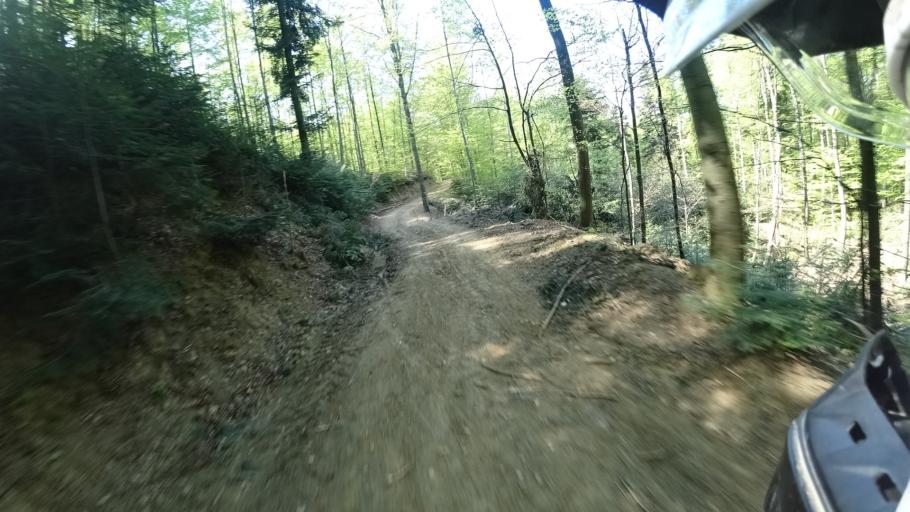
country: HR
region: Zagrebacka
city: Jablanovec
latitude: 45.9038
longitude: 15.9194
